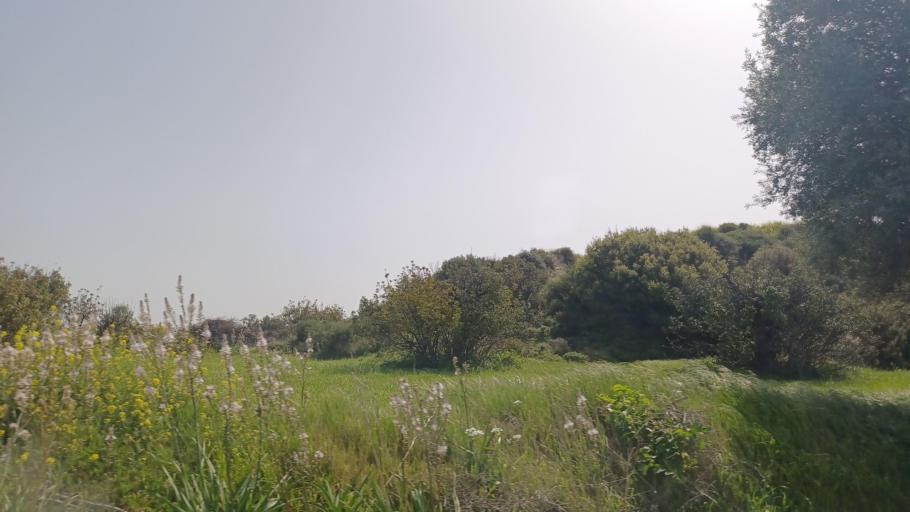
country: CY
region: Limassol
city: Pissouri
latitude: 34.7098
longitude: 32.7091
